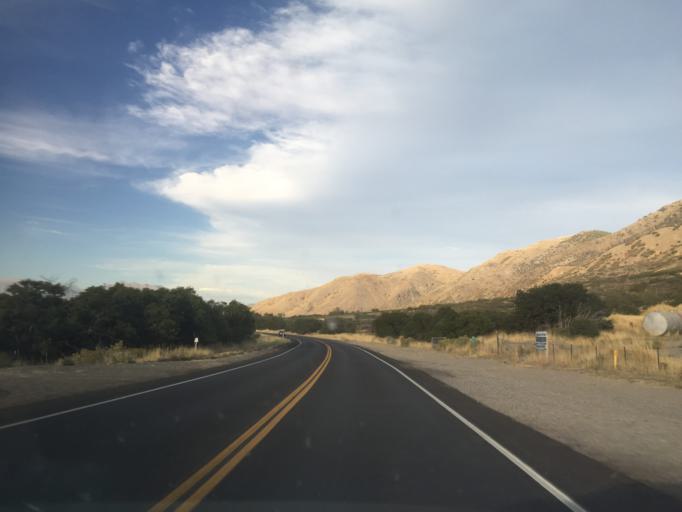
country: US
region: Utah
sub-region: Utah County
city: Santaquin
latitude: 39.9863
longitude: -111.7608
